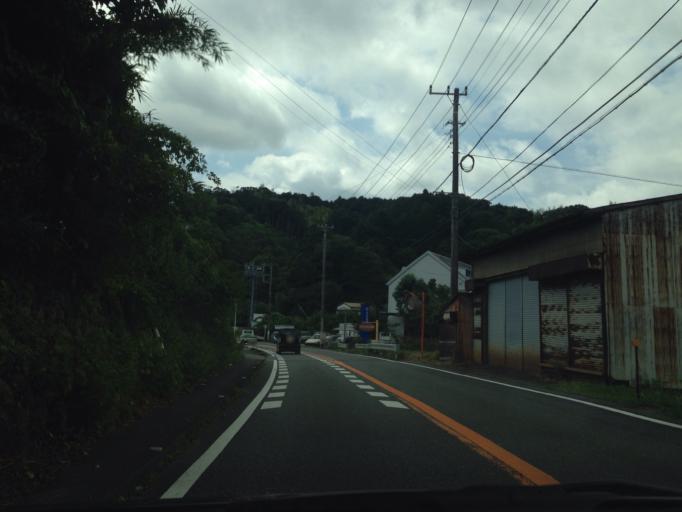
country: JP
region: Shizuoka
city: Shimoda
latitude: 34.6627
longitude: 138.8920
